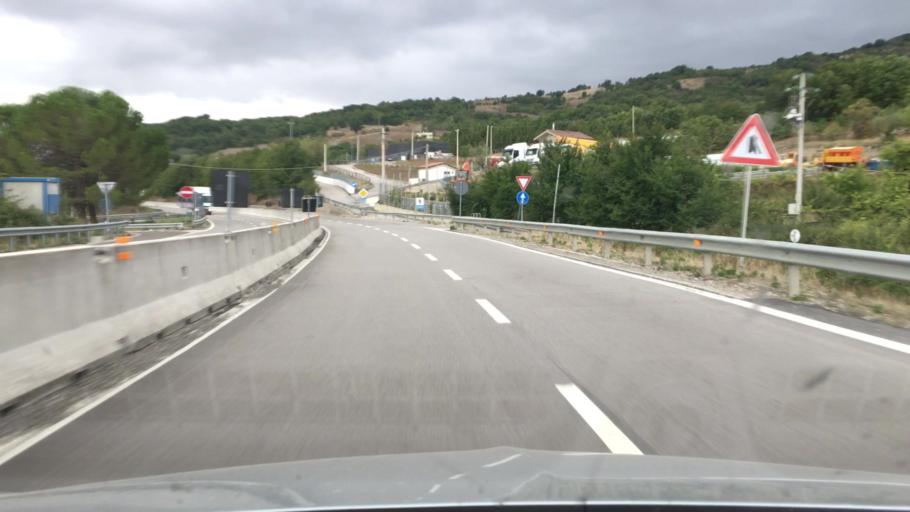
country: IT
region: Basilicate
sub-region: Provincia di Potenza
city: Vaglio Basilicata
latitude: 40.6518
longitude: 15.9266
